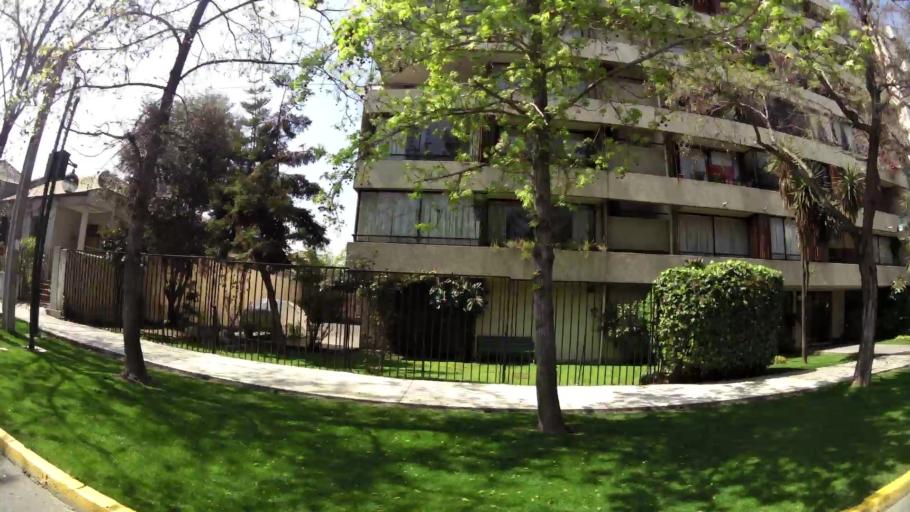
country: CL
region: Santiago Metropolitan
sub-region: Provincia de Santiago
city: Villa Presidente Frei, Nunoa, Santiago, Chile
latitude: -33.4464
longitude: -70.6042
